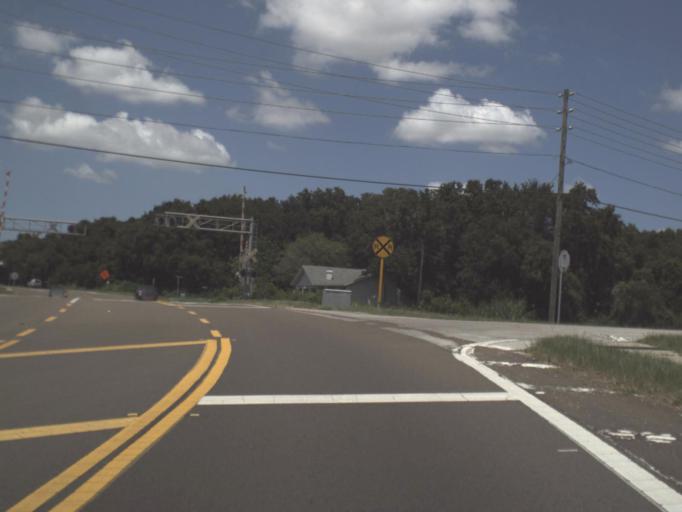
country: US
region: Florida
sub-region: Pinellas County
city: Oldsmar
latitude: 28.0250
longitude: -82.6909
